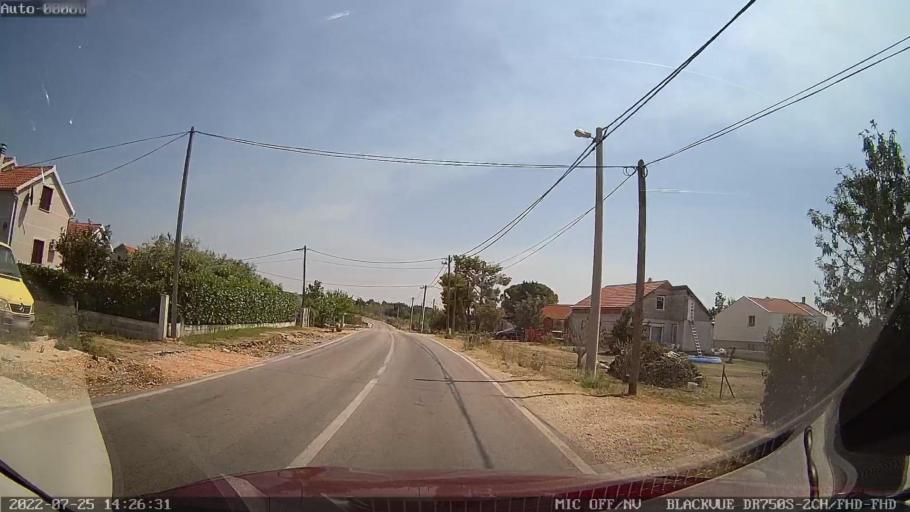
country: HR
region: Zadarska
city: Policnik
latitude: 44.1384
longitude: 15.3387
